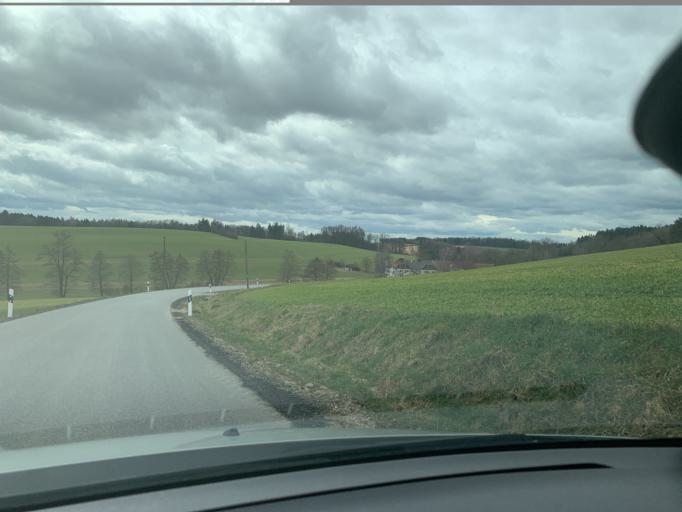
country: DE
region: Bavaria
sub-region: Lower Bavaria
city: Kumhausen
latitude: 48.5185
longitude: 12.1922
